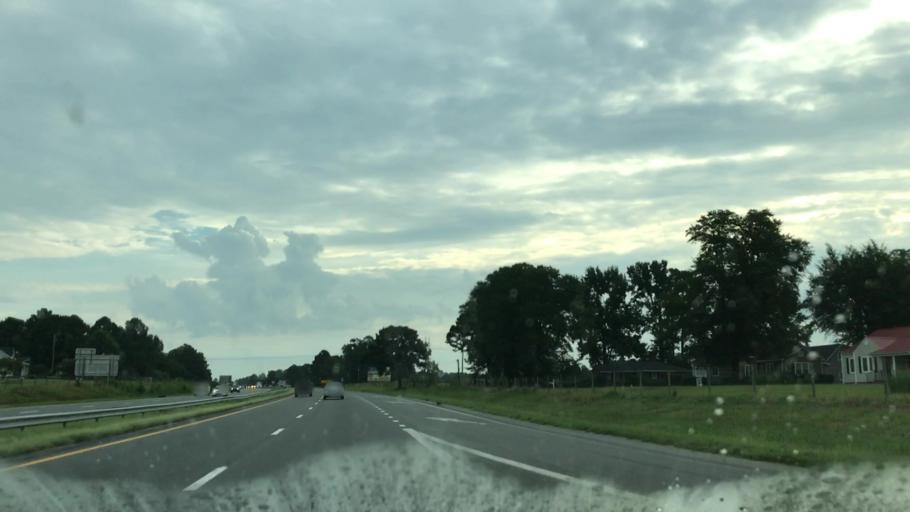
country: US
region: North Carolina
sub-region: Harnett County
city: Dunn
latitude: 35.3188
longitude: -78.5726
